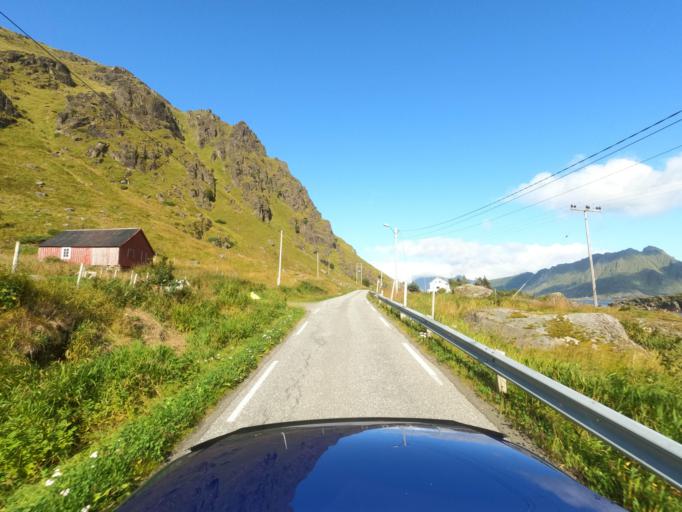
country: NO
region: Nordland
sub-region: Vestvagoy
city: Leknes
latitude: 68.0976
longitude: 13.7246
